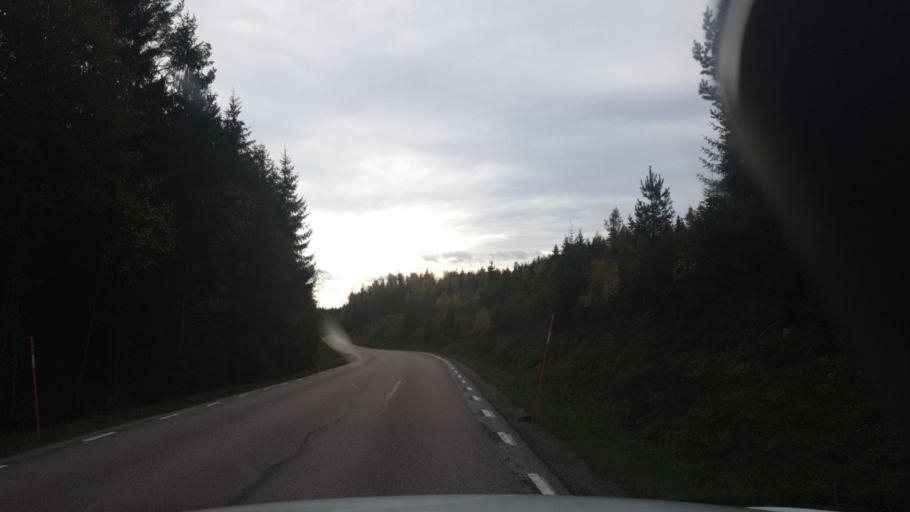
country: SE
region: Vaermland
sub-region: Arvika Kommun
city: Arvika
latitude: 59.6979
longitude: 12.7918
